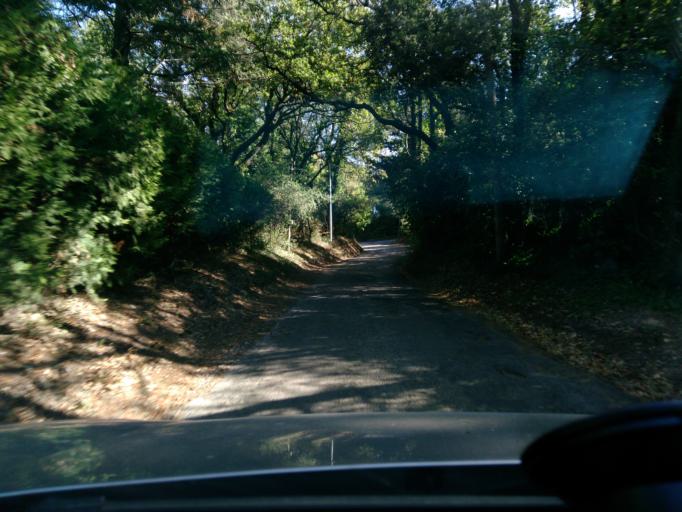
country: FR
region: Rhone-Alpes
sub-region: Departement de la Drome
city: Montboucher-sur-Jabron
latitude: 44.5539
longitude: 4.7782
